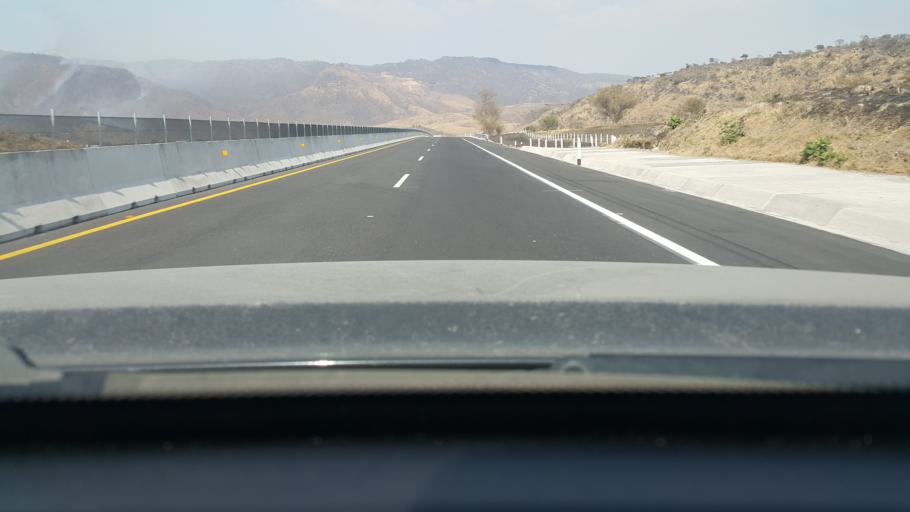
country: MX
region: Nayarit
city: Jala
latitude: 21.0762
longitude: -104.4440
